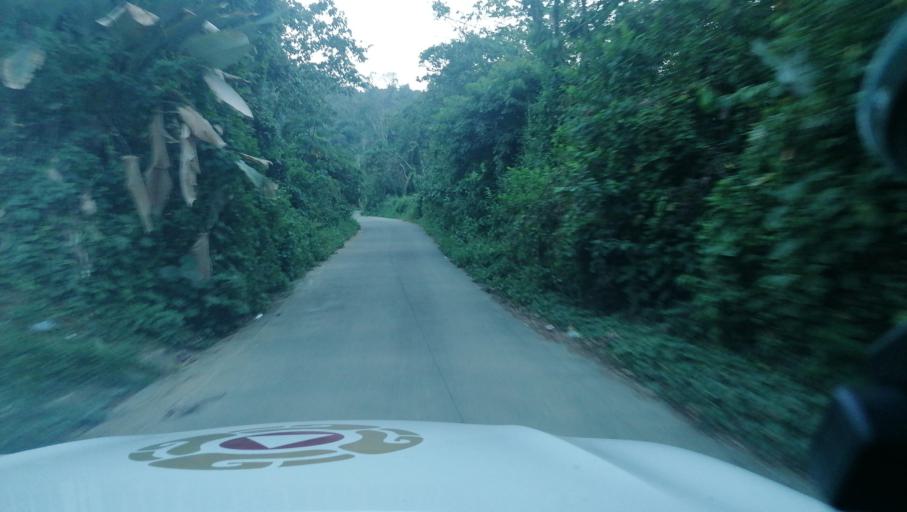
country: MX
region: Chiapas
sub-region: Cacahoatan
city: Benito Juarez
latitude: 15.0543
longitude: -92.2431
